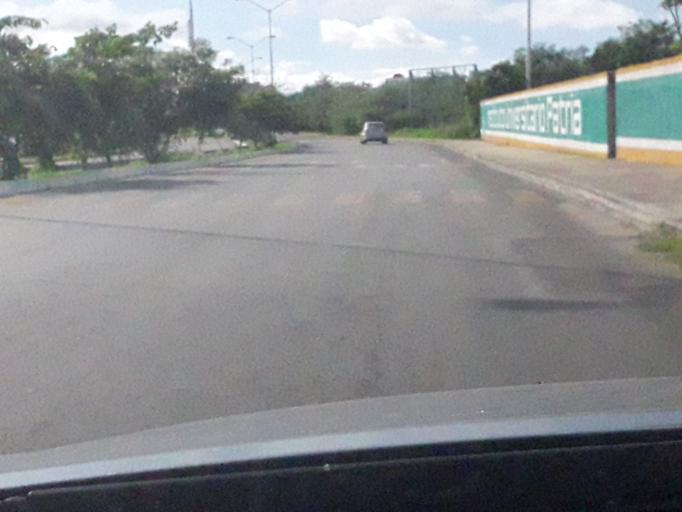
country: MX
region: Yucatan
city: Merida
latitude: 21.0372
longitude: -89.6086
